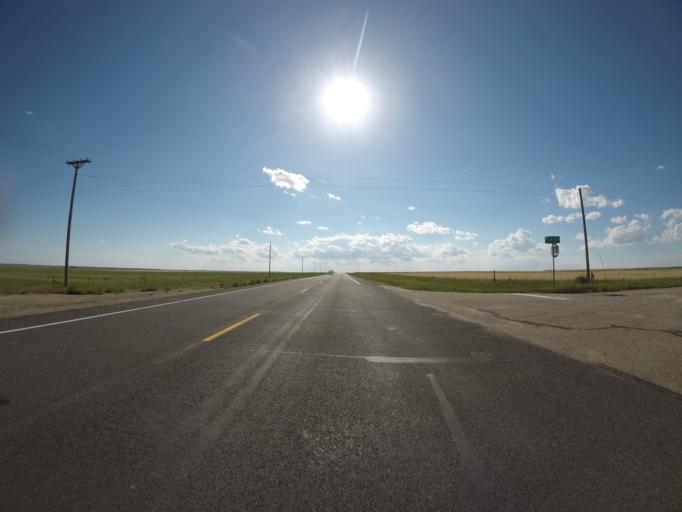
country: US
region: Colorado
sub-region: Morgan County
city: Fort Morgan
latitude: 40.6110
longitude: -103.7723
